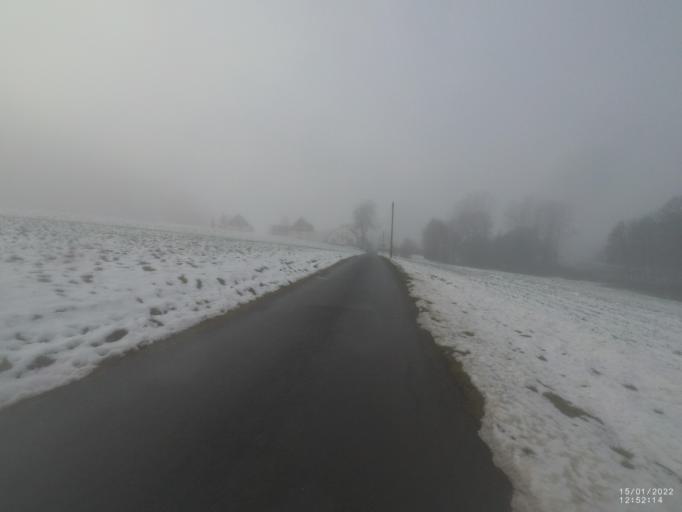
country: DE
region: North Rhine-Westphalia
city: Kierspe
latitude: 51.1104
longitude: 7.6088
